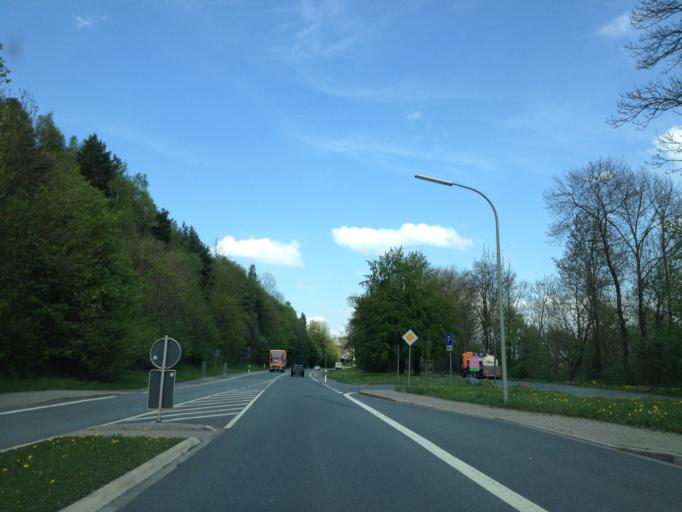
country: DE
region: North Rhine-Westphalia
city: Warstein
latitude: 51.4830
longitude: 8.2568
